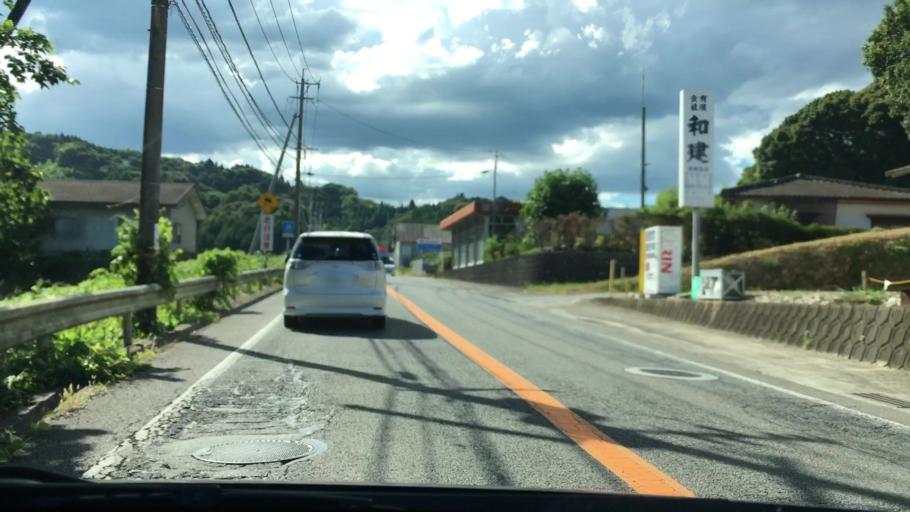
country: JP
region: Saga Prefecture
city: Takeocho-takeo
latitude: 33.1848
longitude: 129.9907
